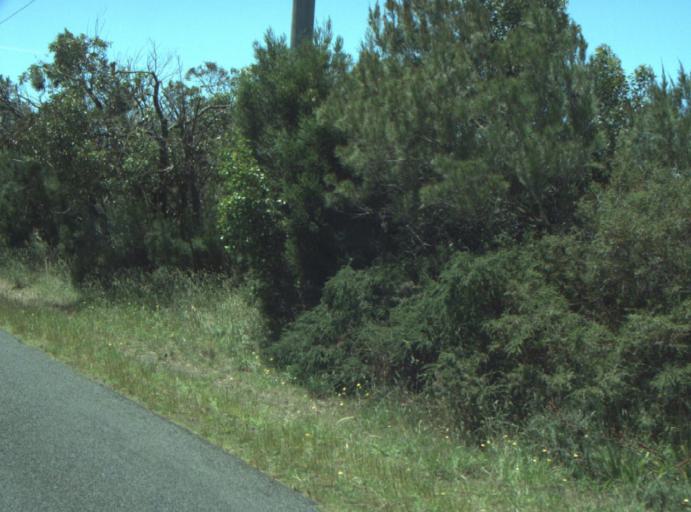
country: AU
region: Victoria
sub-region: Greater Geelong
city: Clifton Springs
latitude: -38.2400
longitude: 144.5744
